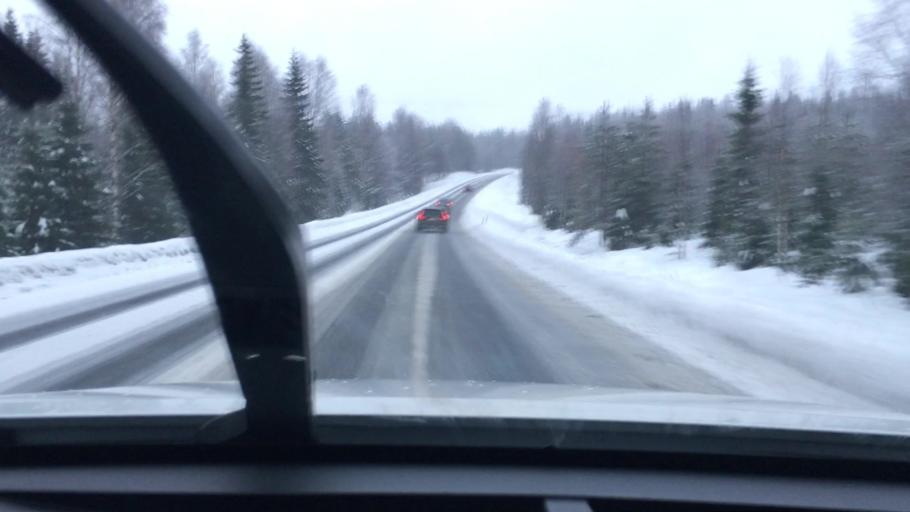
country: FI
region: Northern Savo
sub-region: Ylae-Savo
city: Sonkajaervi
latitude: 63.7693
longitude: 27.4144
